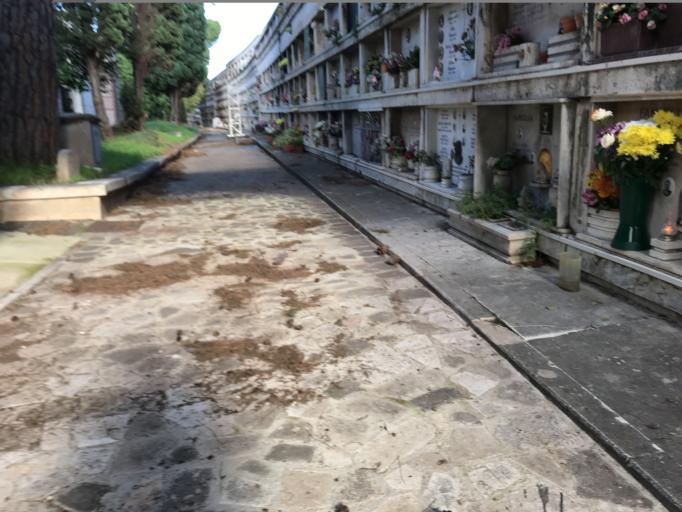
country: IT
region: Latium
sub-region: Citta metropolitana di Roma Capitale
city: Rome
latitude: 41.9055
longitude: 12.5323
